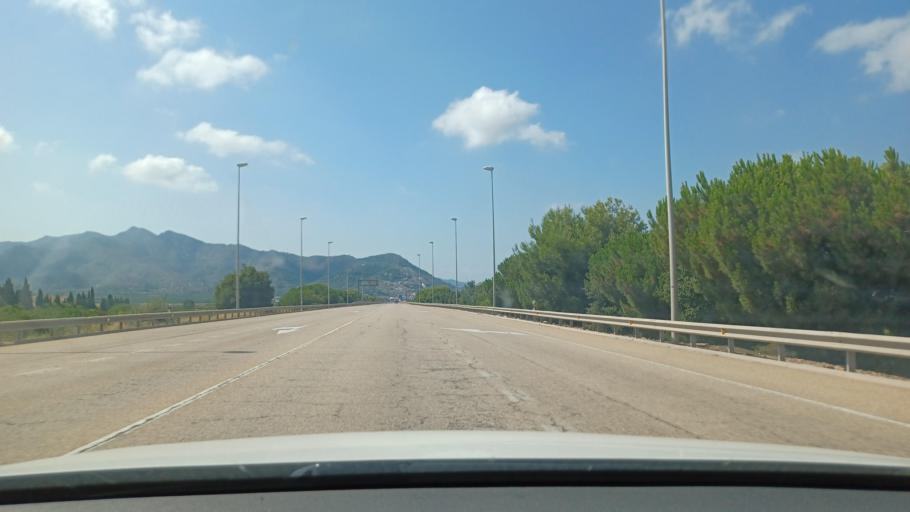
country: ES
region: Valencia
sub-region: Provincia de Castello
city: Villavieja
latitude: 39.8372
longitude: -0.1686
